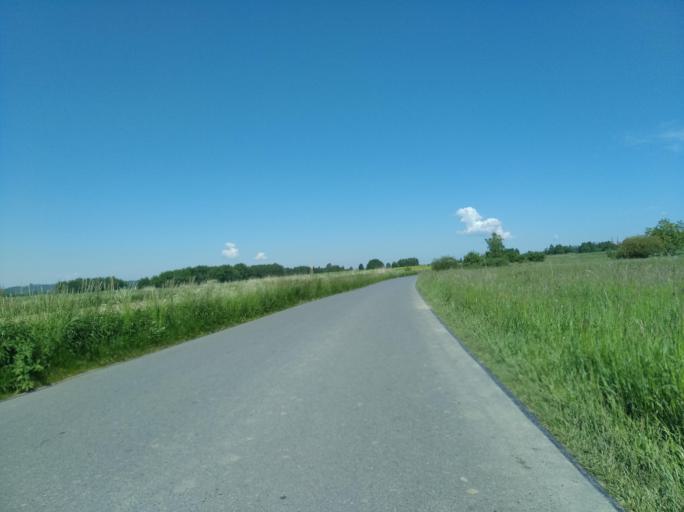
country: PL
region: Subcarpathian Voivodeship
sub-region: Powiat krosnienski
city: Odrzykon
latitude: 49.7279
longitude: 21.7548
